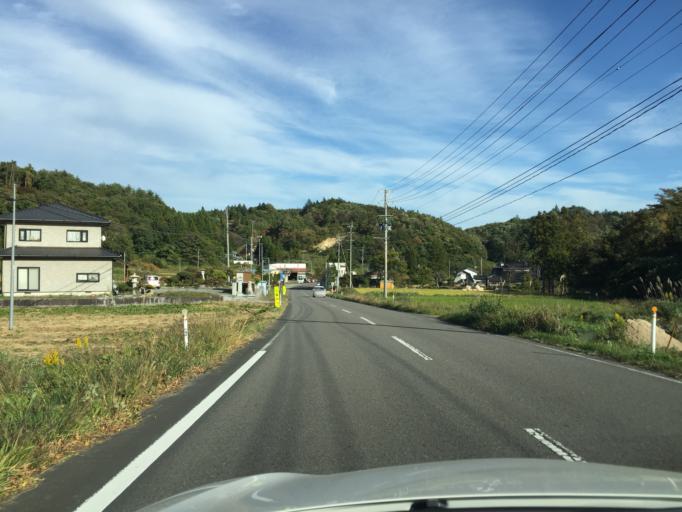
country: JP
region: Fukushima
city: Funehikimachi-funehiki
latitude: 37.3300
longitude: 140.5875
